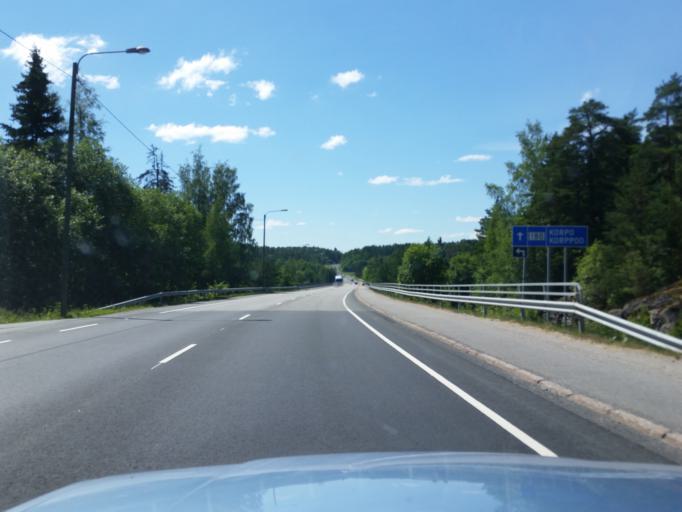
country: FI
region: Varsinais-Suomi
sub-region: Aboland-Turunmaa
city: Pargas
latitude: 60.3252
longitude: 22.3459
